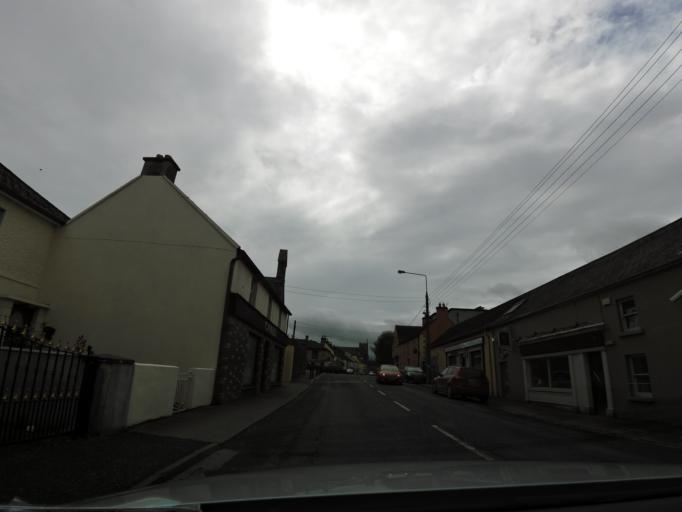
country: IE
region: Leinster
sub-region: Kilkenny
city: Ballyragget
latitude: 52.7331
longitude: -7.3981
